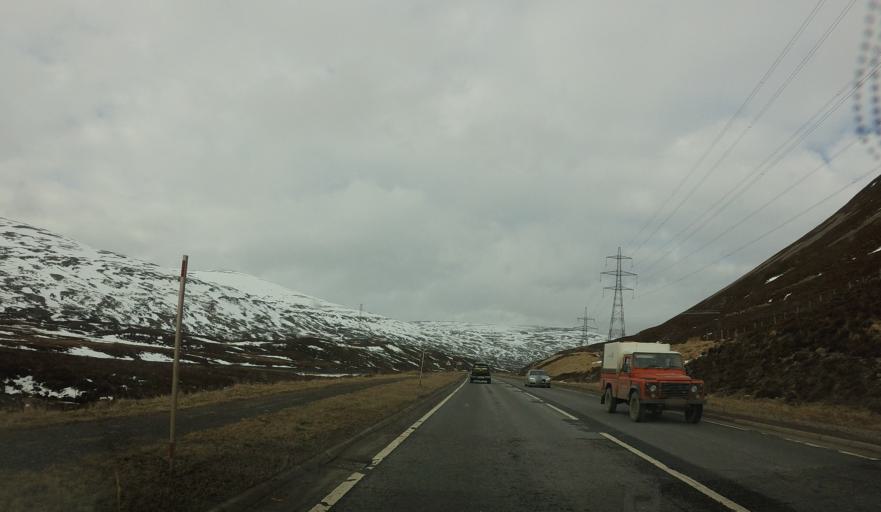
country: GB
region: Scotland
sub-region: Highland
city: Kingussie
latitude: 56.8645
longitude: -4.2527
